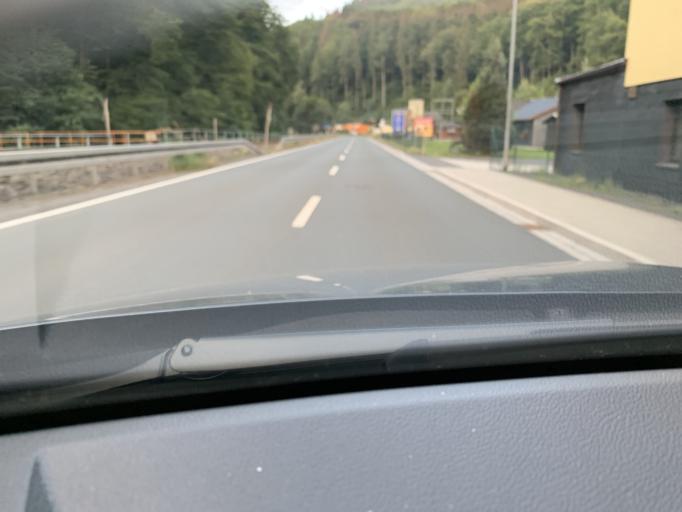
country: DE
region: Thuringia
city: Judenbach
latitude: 50.3950
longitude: 11.2009
